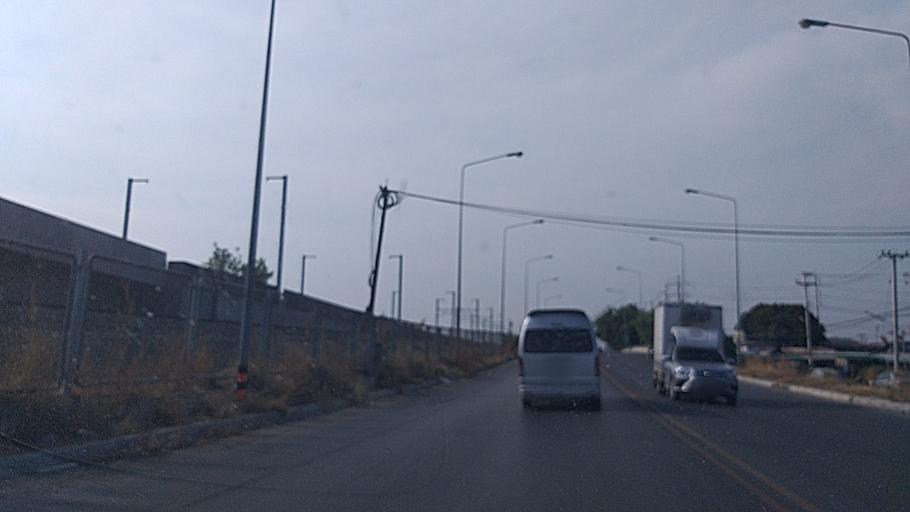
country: TH
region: Phra Nakhon Si Ayutthaya
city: Ban Bang Kadi Pathum Thani
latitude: 13.9817
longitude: 100.6031
